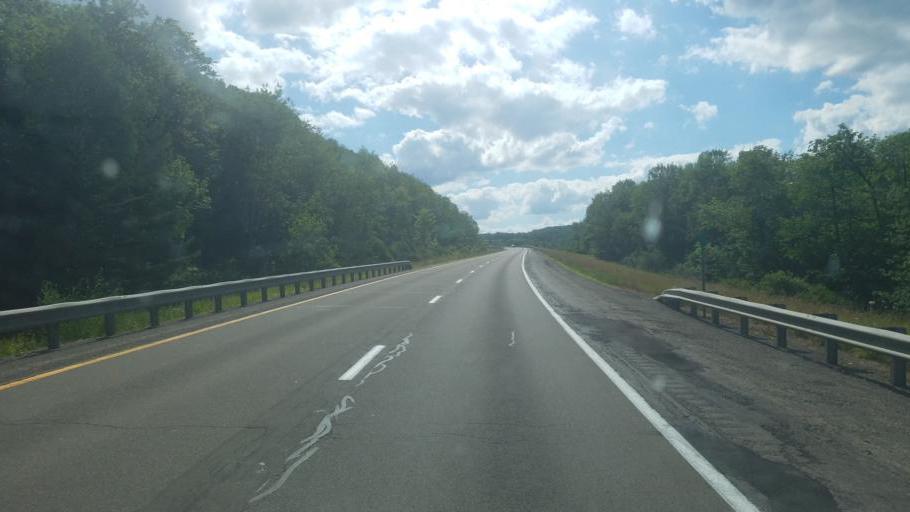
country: US
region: New York
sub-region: Allegany County
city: Alfred
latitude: 42.3169
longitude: -77.8458
